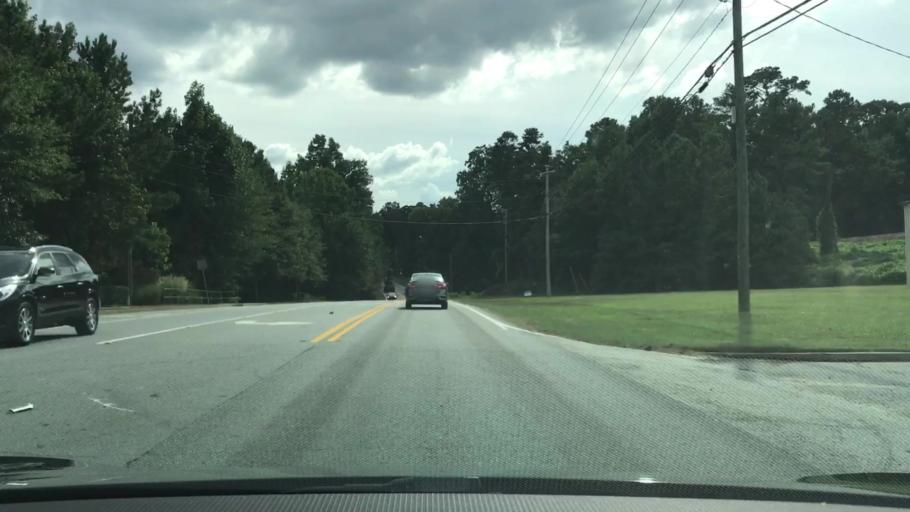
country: US
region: Georgia
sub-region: Gwinnett County
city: Suwanee
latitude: 34.0712
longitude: -84.0554
